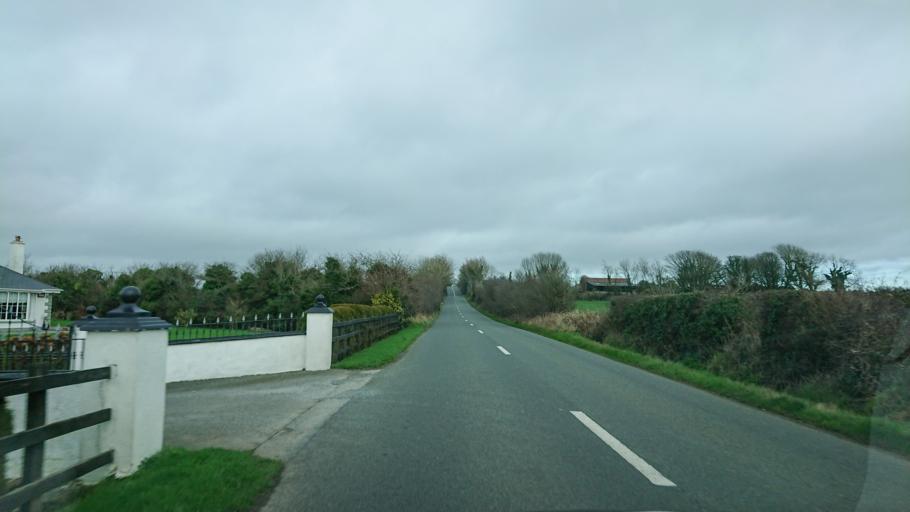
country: IE
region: Munster
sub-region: Waterford
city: Portlaw
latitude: 52.1890
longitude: -7.2871
